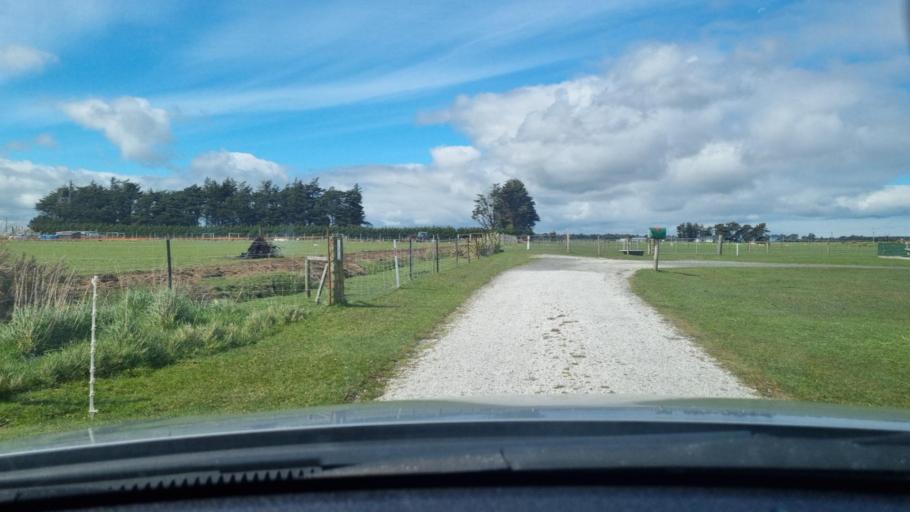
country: NZ
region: Southland
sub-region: Invercargill City
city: Invercargill
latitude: -46.4774
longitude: 168.3928
